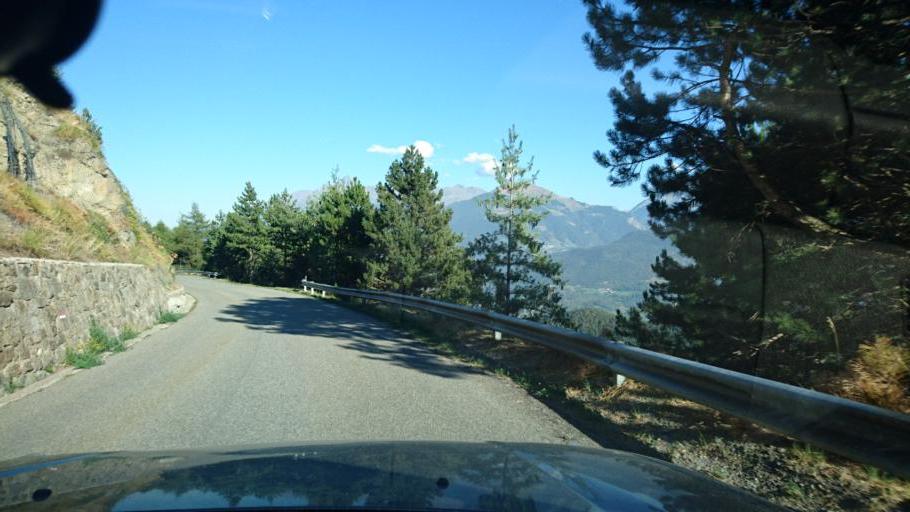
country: IT
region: Aosta Valley
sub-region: Valle d'Aosta
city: Saint-Nicolas
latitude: 45.7191
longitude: 7.1527
